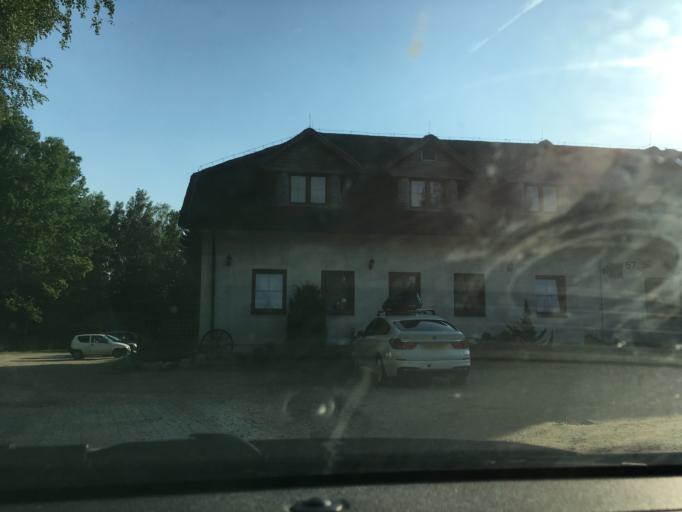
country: PL
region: Podlasie
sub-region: Powiat moniecki
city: Monki
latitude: 53.4118
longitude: 22.7803
